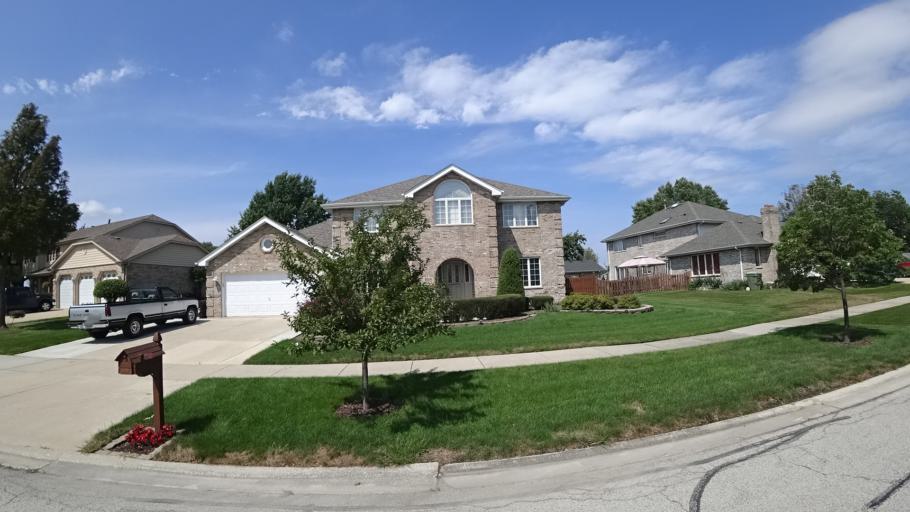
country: US
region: Illinois
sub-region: Cook County
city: Orland Hills
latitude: 41.5662
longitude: -87.8202
